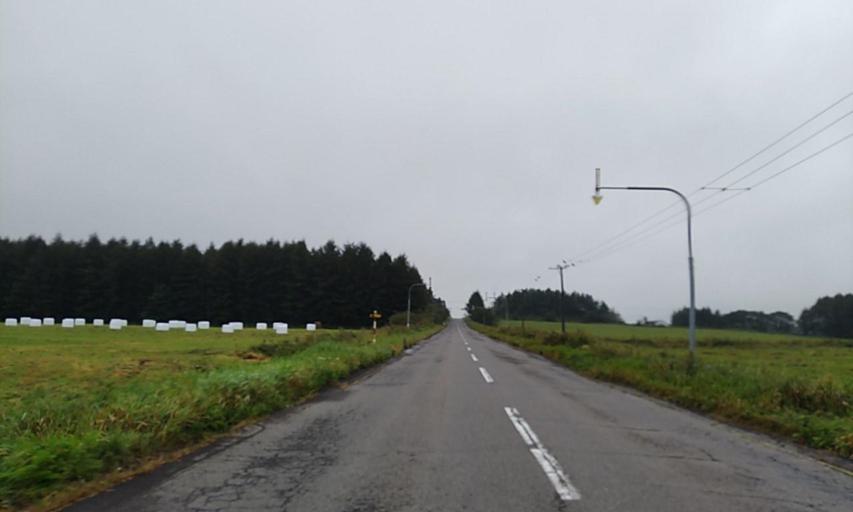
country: JP
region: Hokkaido
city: Shibetsu
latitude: 43.5086
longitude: 144.6673
